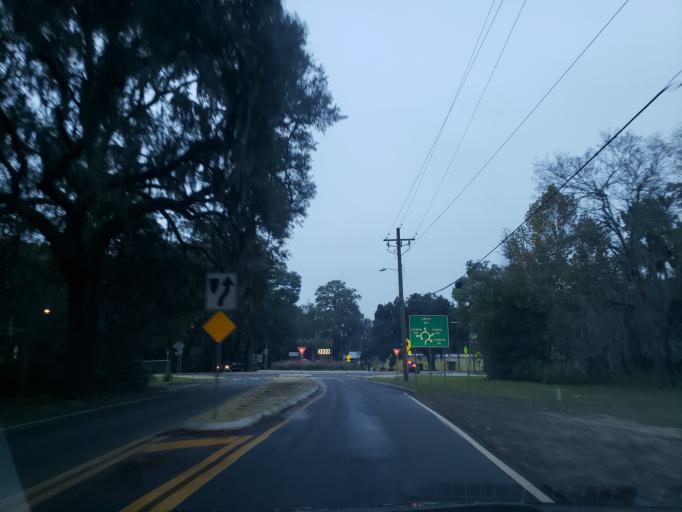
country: US
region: Georgia
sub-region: Chatham County
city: Thunderbolt
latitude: 32.0146
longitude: -81.0658
